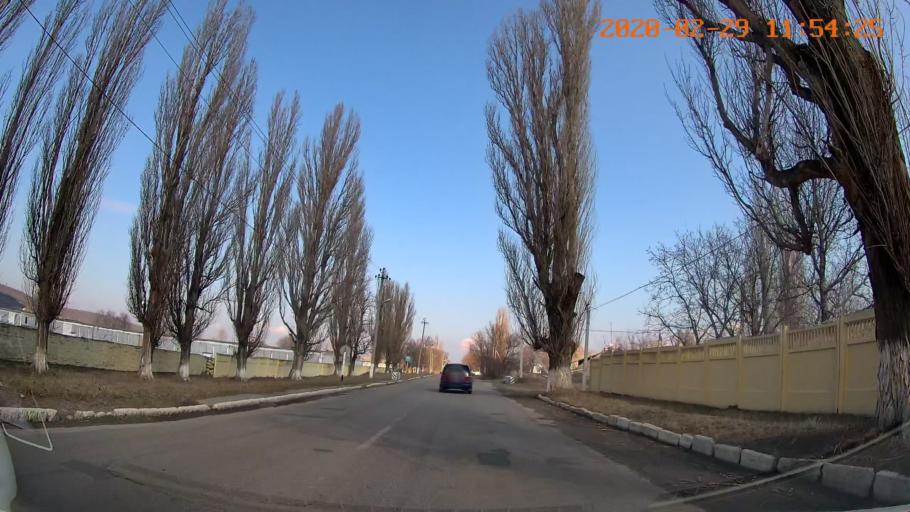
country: MD
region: Telenesti
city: Ribnita
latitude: 47.7842
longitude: 28.9950
